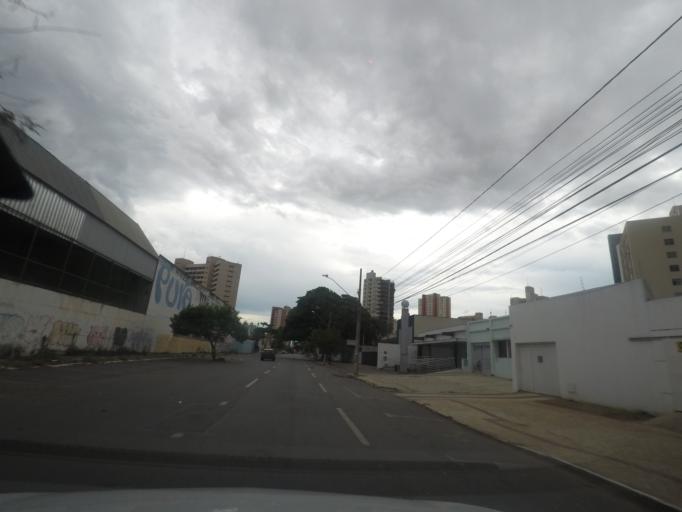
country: BR
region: Goias
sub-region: Goiania
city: Goiania
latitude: -16.6777
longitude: -49.2636
